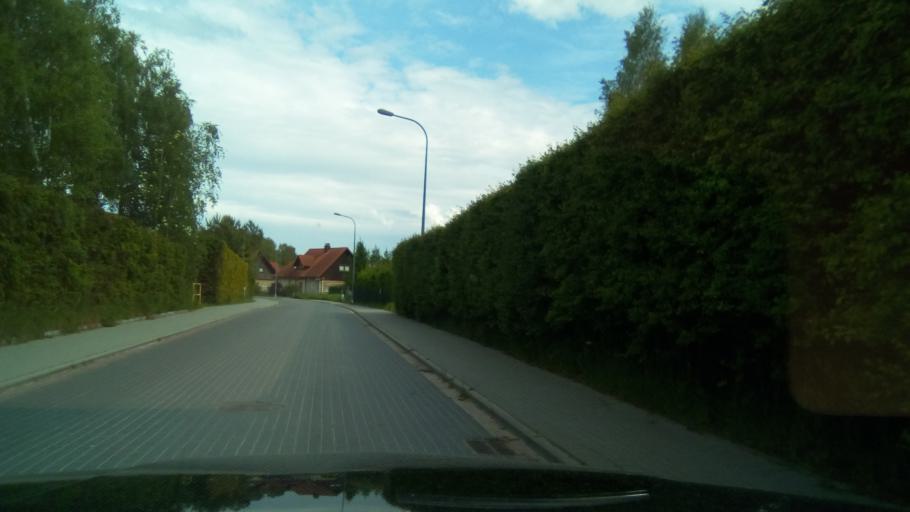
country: PL
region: Pomeranian Voivodeship
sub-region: Powiat pucki
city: Wierzchucino
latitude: 54.8259
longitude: 18.0784
